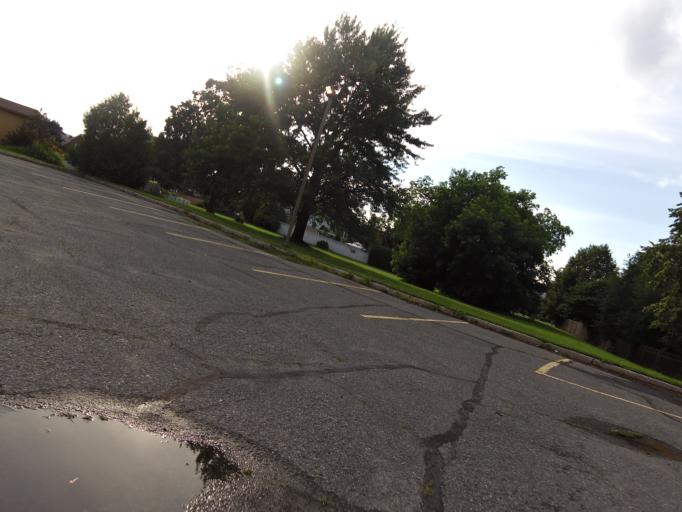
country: CA
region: Ontario
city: Bells Corners
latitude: 45.3264
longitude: -75.7739
